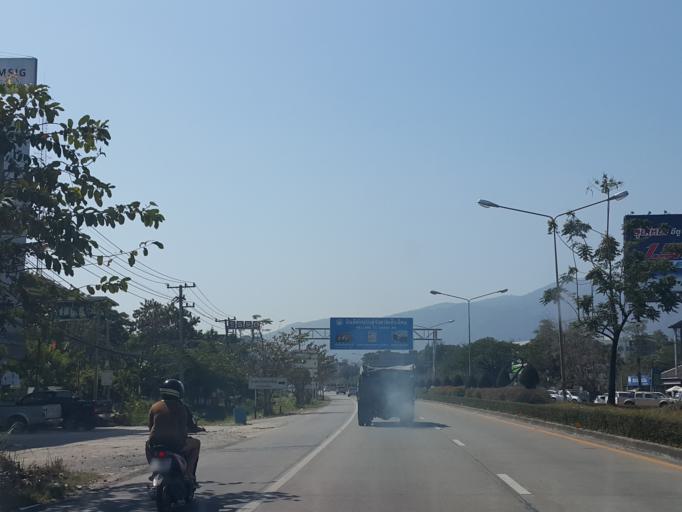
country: TH
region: Chiang Mai
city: Chiang Mai
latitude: 18.8100
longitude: 98.9763
